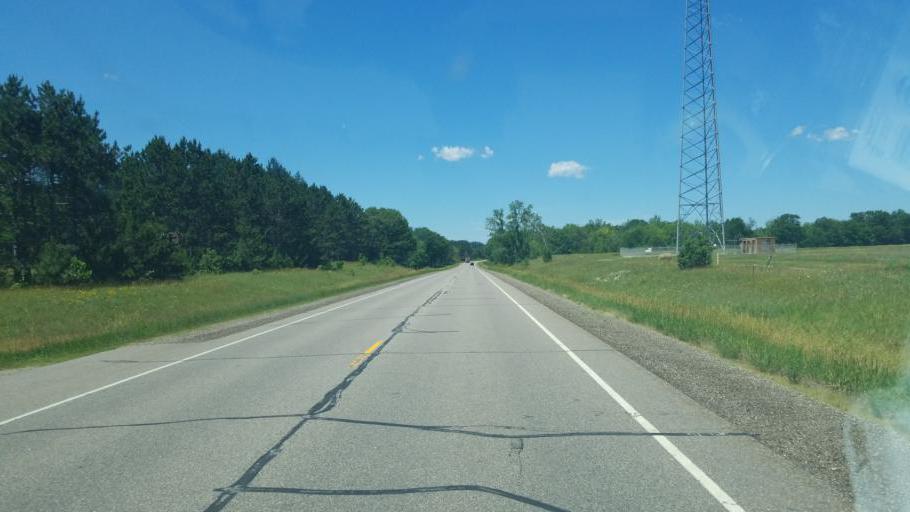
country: US
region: Wisconsin
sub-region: Adams County
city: Friendship
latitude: 44.0468
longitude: -89.9821
